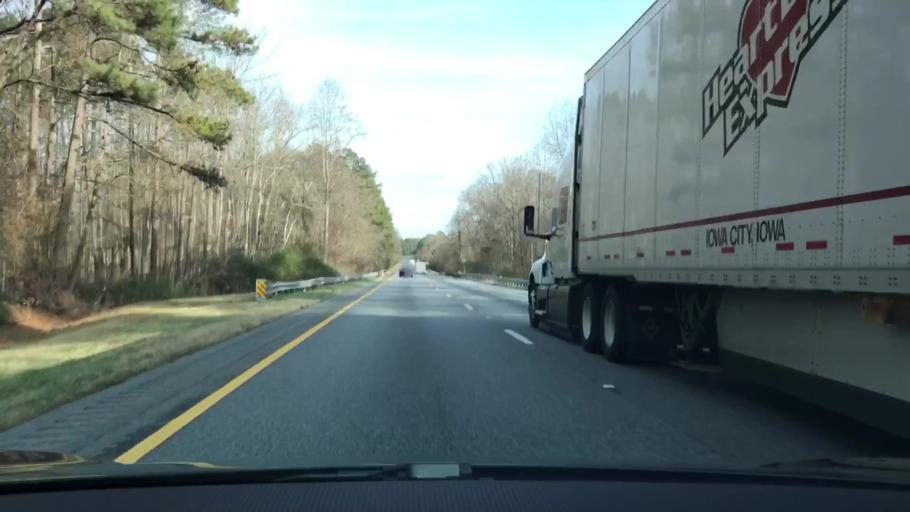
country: US
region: Georgia
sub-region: Morgan County
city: Madison
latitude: 33.5766
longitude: -83.5525
